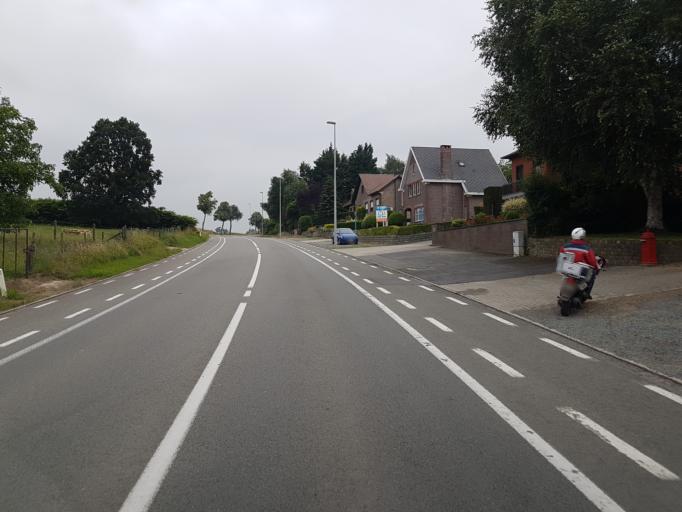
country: BE
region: Flanders
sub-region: Provincie Oost-Vlaanderen
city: Haaltert
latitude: 50.8612
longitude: 3.9600
